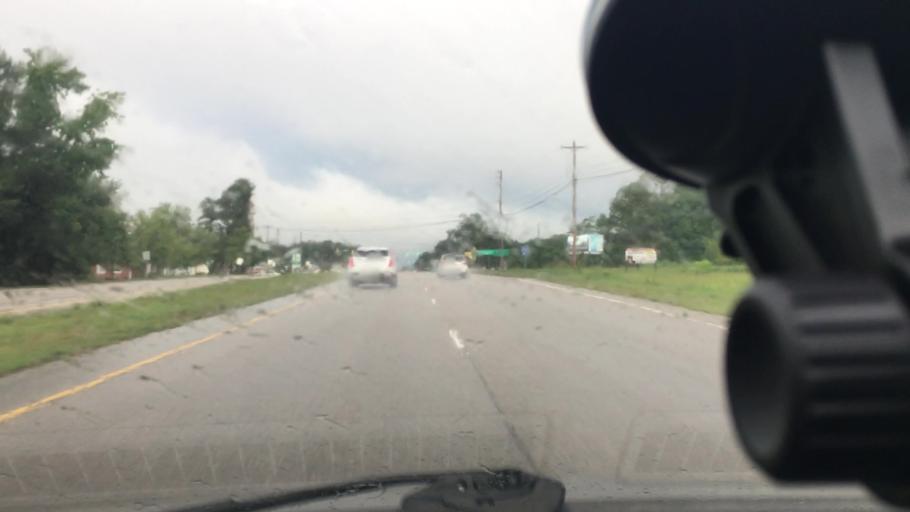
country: US
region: North Carolina
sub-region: Wilson County
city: Wilson
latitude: 35.7641
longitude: -78.0119
